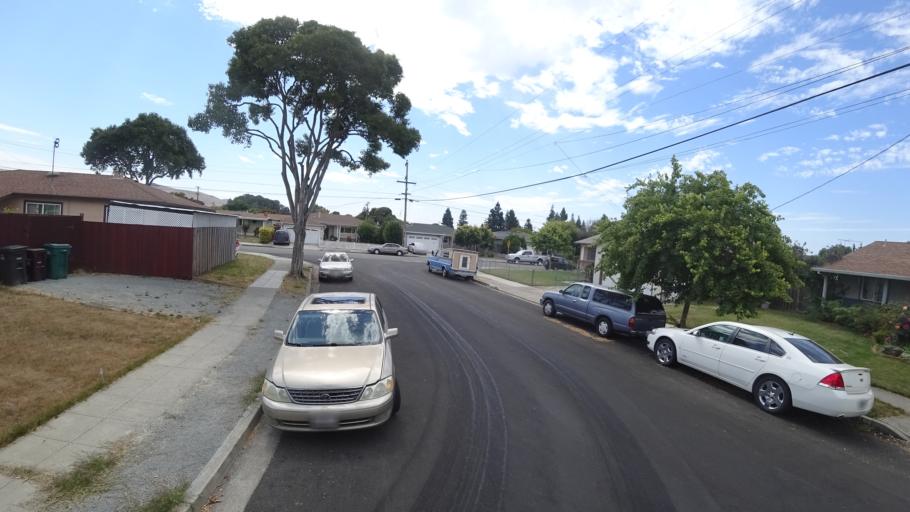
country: US
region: California
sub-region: Alameda County
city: Hayward
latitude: 37.6442
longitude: -122.0789
